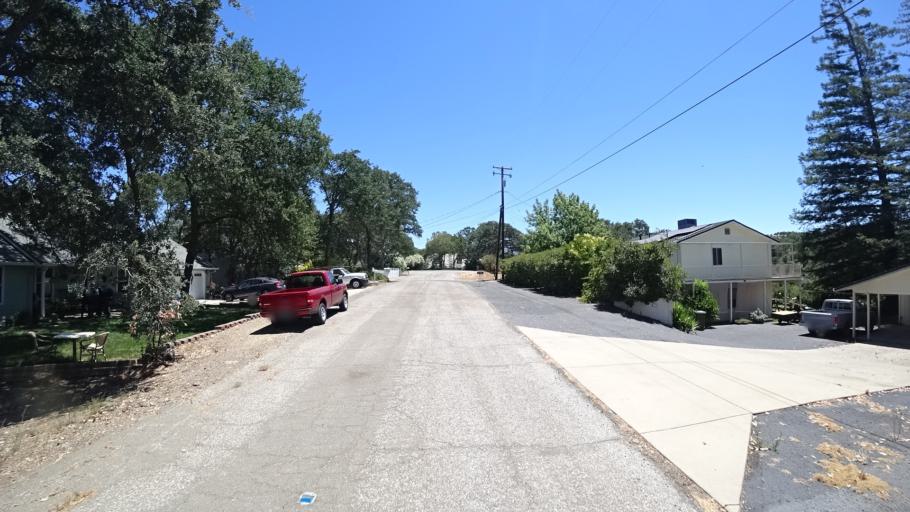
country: US
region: California
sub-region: Calaveras County
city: Rancho Calaveras
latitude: 38.1513
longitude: -120.8347
